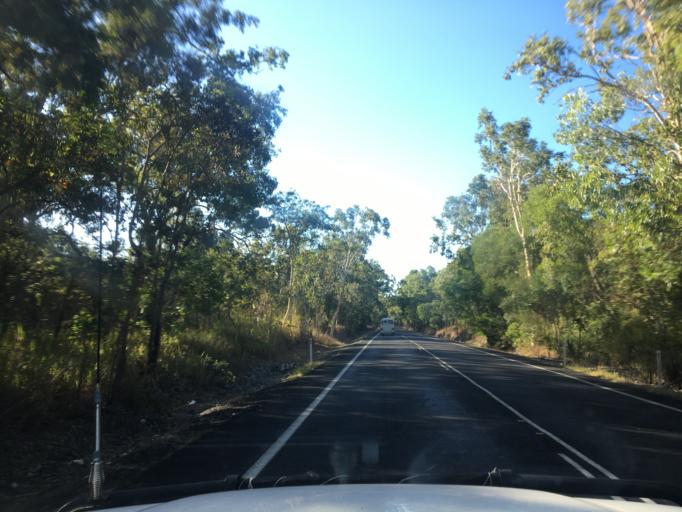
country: AU
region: Queensland
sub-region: Cairns
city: Palm Cove
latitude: -16.6718
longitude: 145.5680
